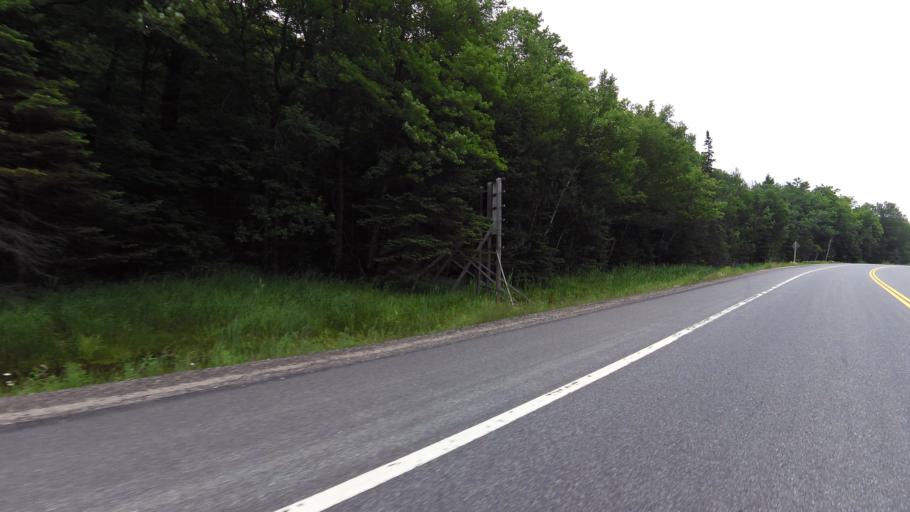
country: CA
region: Ontario
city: Huntsville
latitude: 45.3565
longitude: -78.9315
